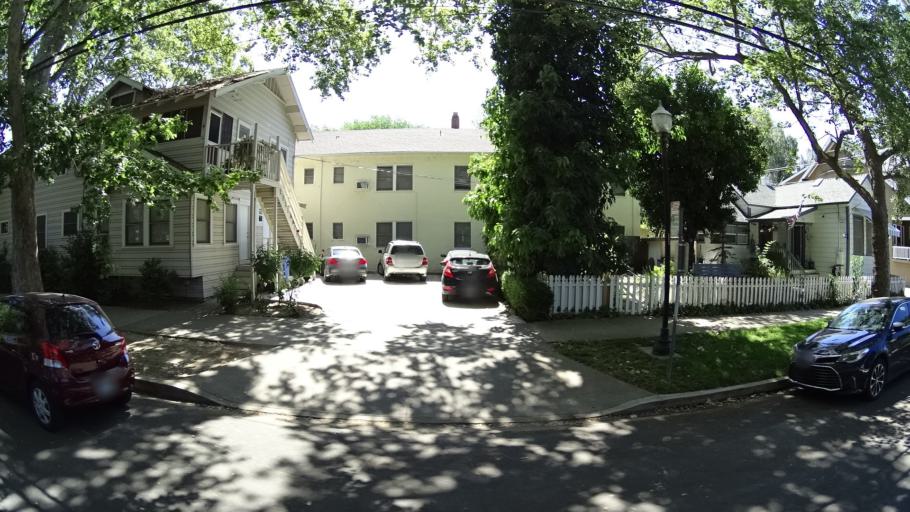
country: US
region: California
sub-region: Sacramento County
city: Sacramento
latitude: 38.5777
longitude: -121.4765
